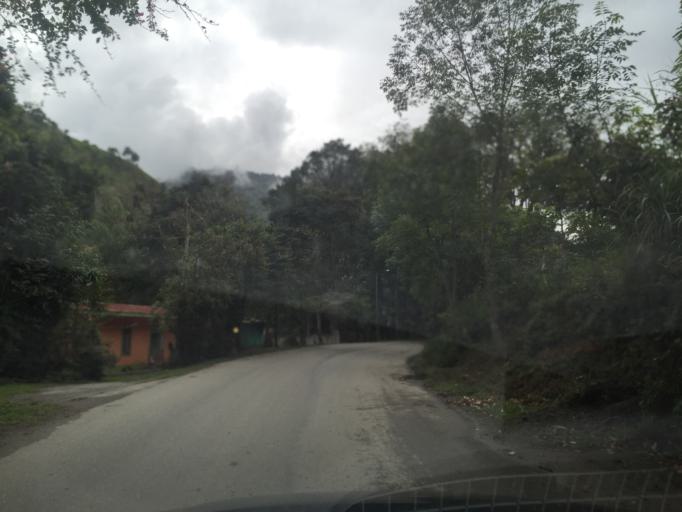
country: CO
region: Tolima
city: Cajamarca
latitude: 4.3997
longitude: -75.4415
